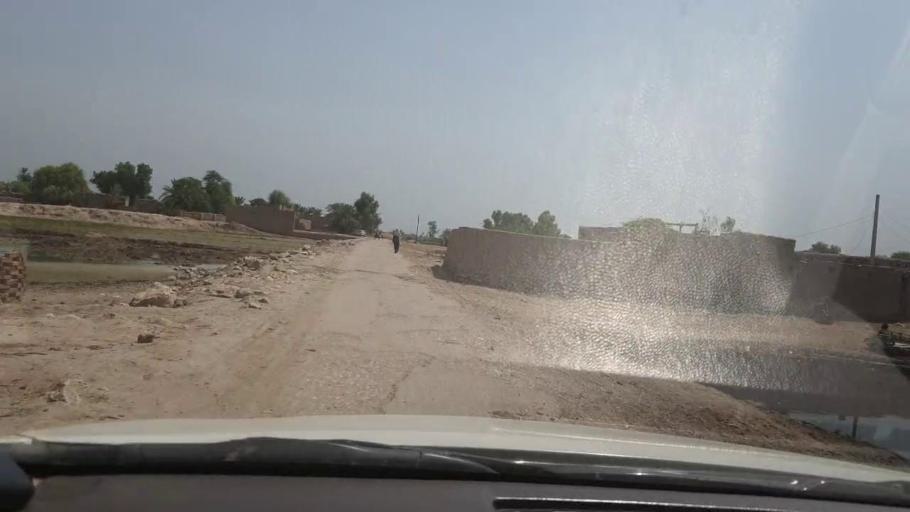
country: PK
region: Sindh
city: Shikarpur
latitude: 27.9438
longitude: 68.5975
